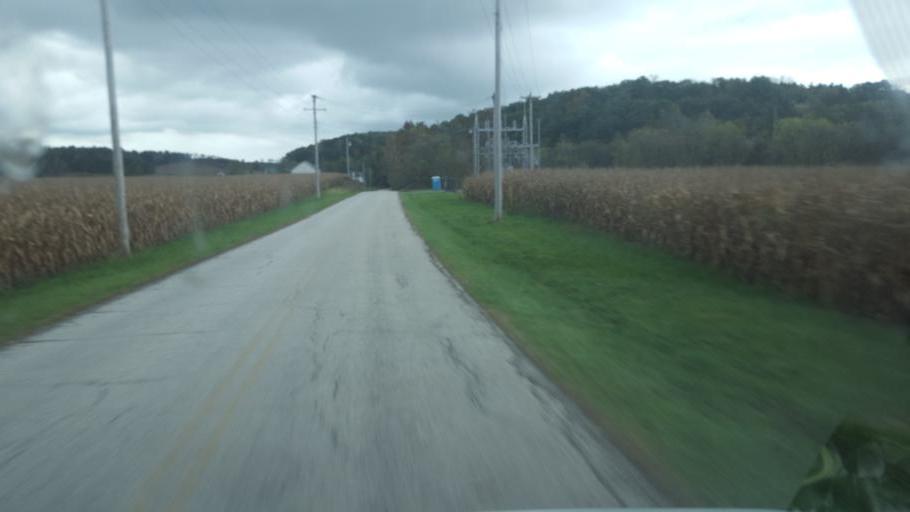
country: US
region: Ohio
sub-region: Ashland County
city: Loudonville
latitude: 40.5908
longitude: -82.1679
